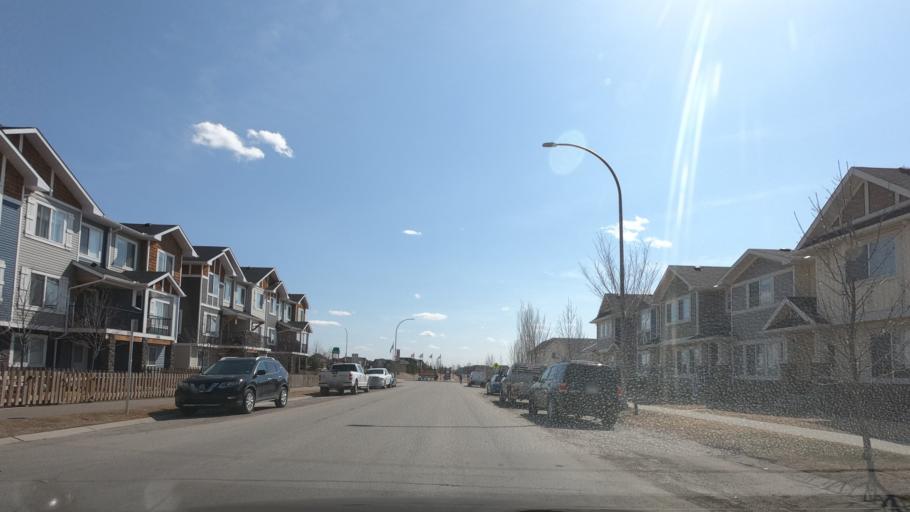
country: CA
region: Alberta
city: Airdrie
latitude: 51.2680
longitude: -113.9817
